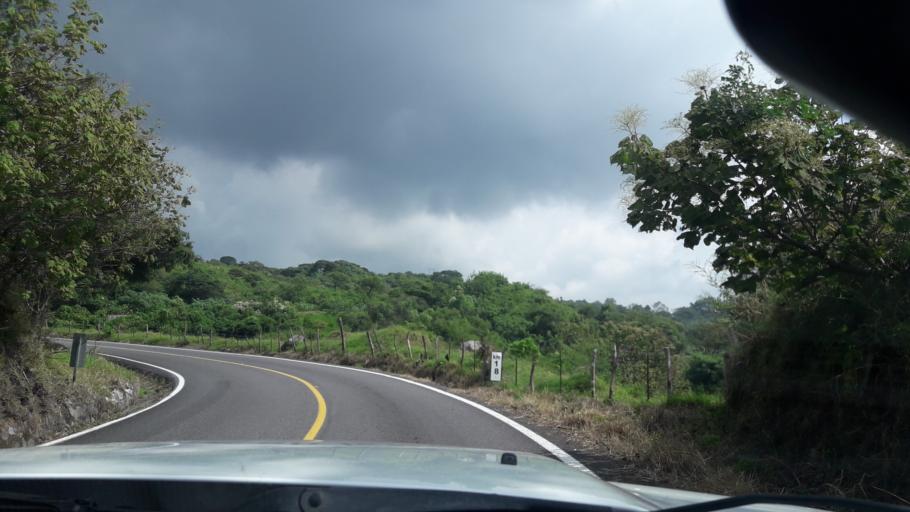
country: MX
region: Colima
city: Suchitlan
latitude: 19.4362
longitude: -103.7107
